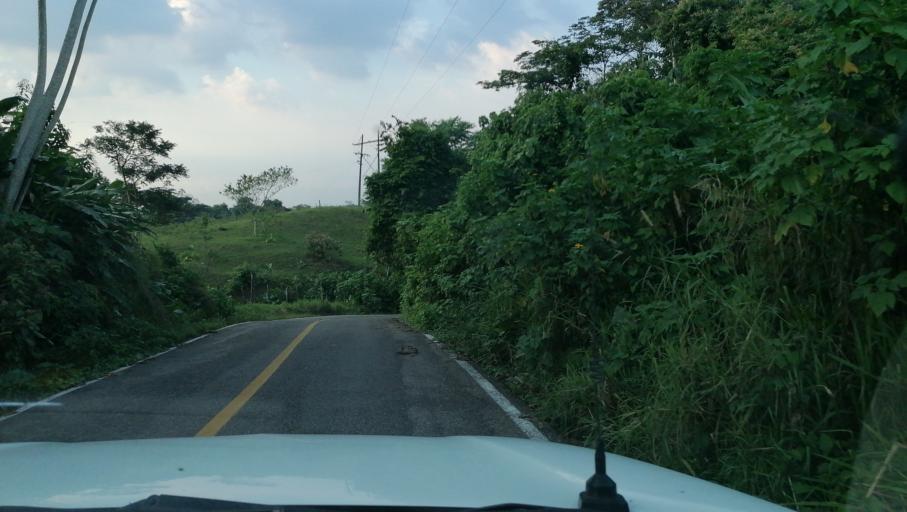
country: MX
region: Chiapas
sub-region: Juarez
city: El Triunfo 1ra. Seccion (Cardona)
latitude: 17.4984
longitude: -93.2458
